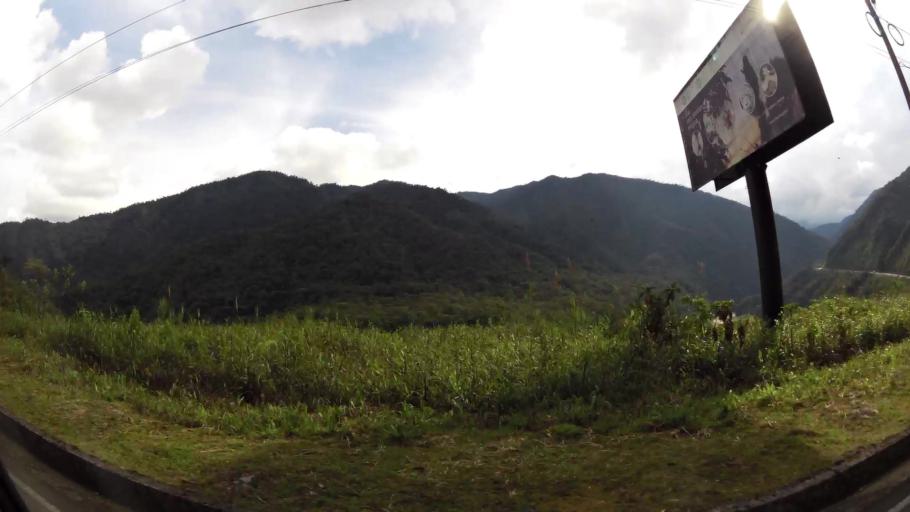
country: EC
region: Pastaza
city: Puyo
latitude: -1.4464
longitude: -78.1615
